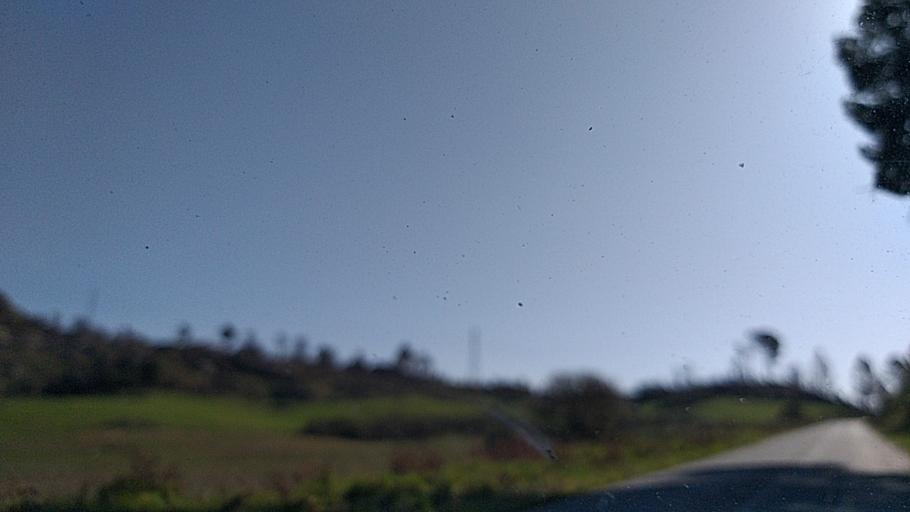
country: PT
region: Guarda
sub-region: Celorico da Beira
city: Celorico da Beira
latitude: 40.6900
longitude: -7.4203
